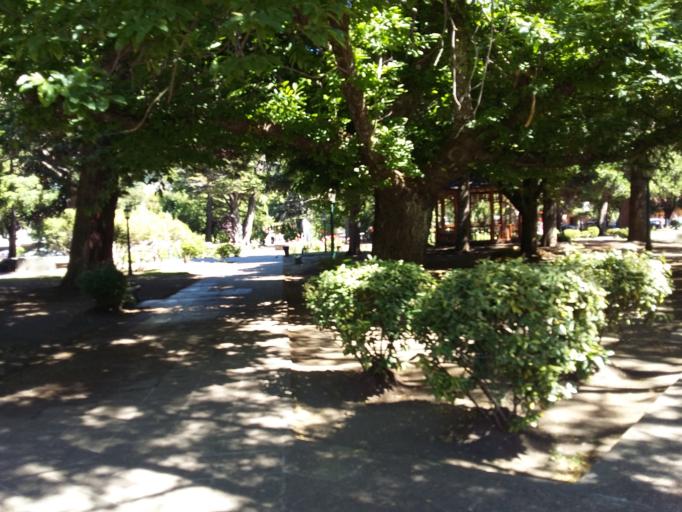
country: AR
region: Neuquen
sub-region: Departamento de Lacar
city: San Martin de los Andes
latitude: -40.1557
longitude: -71.3471
